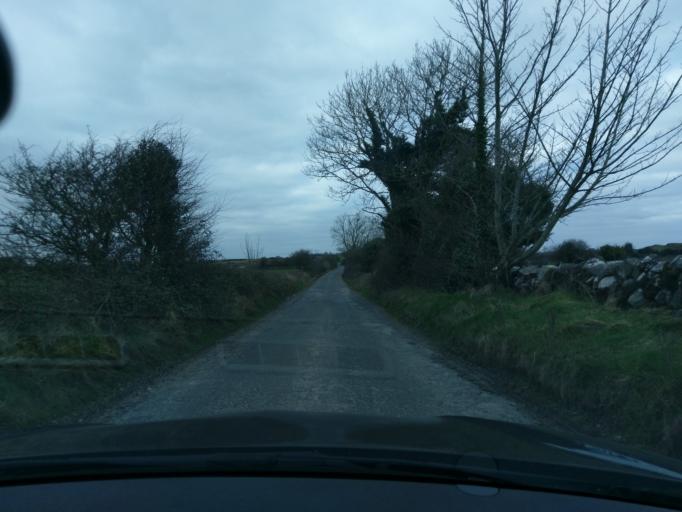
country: IE
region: Connaught
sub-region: County Galway
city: Gort
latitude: 53.1538
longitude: -8.8489
